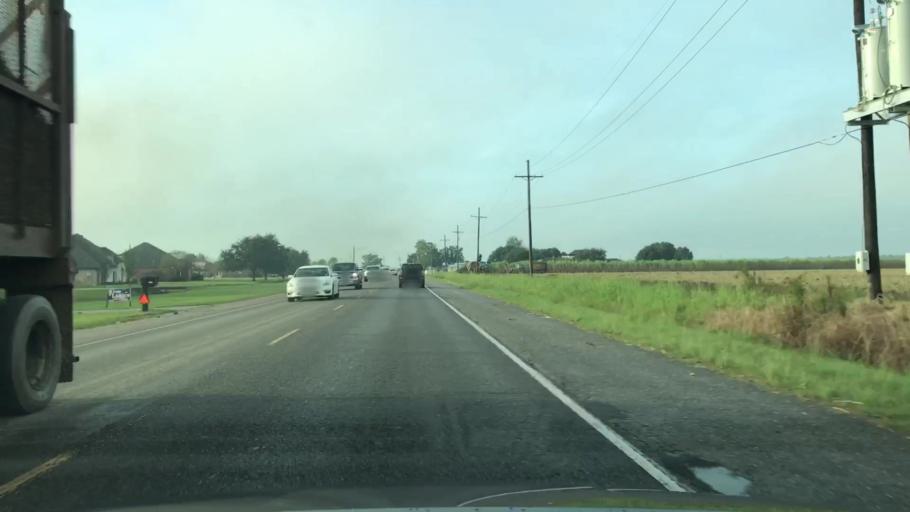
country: US
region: Louisiana
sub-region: Terrebonne Parish
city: Gray
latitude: 29.6679
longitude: -90.8180
